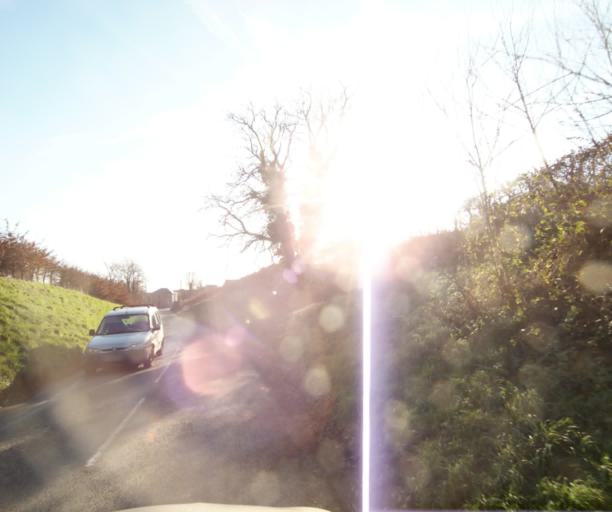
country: FR
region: Nord-Pas-de-Calais
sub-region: Departement du Nord
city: Preseau
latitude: 50.3170
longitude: 3.5746
